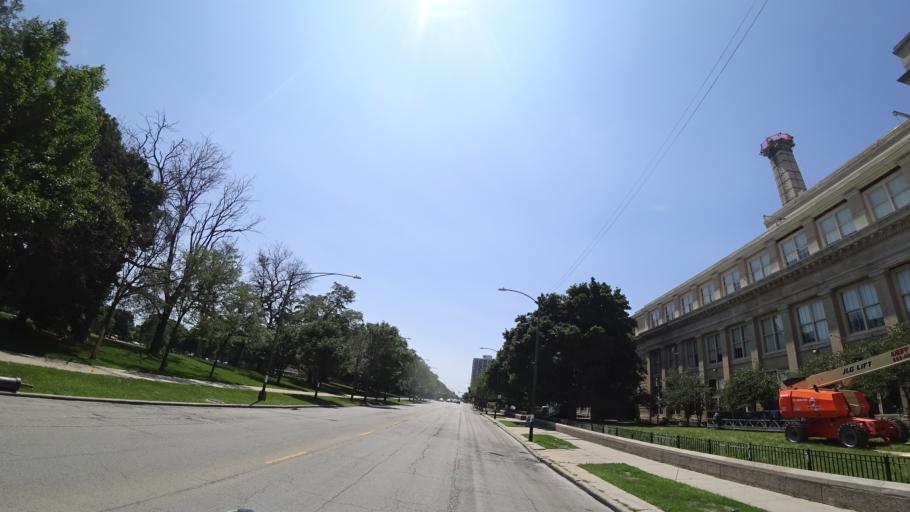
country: US
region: Illinois
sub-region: Cook County
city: Chicago
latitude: 41.7823
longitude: -87.5866
